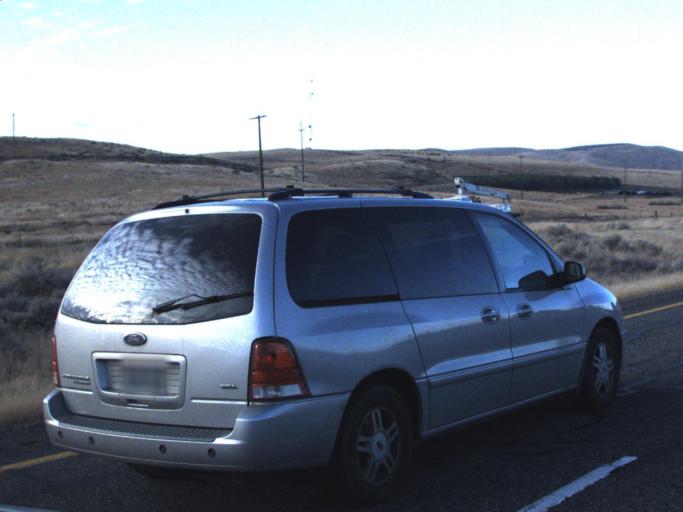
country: US
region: Washington
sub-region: Benton County
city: Prosser
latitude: 46.2164
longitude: -119.7227
